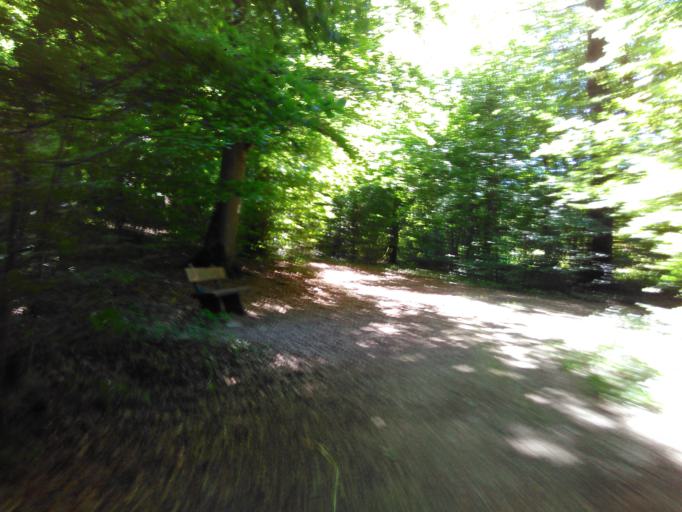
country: LU
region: Luxembourg
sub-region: Canton d'Esch-sur-Alzette
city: Leudelange
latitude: 49.5608
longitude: 6.0584
